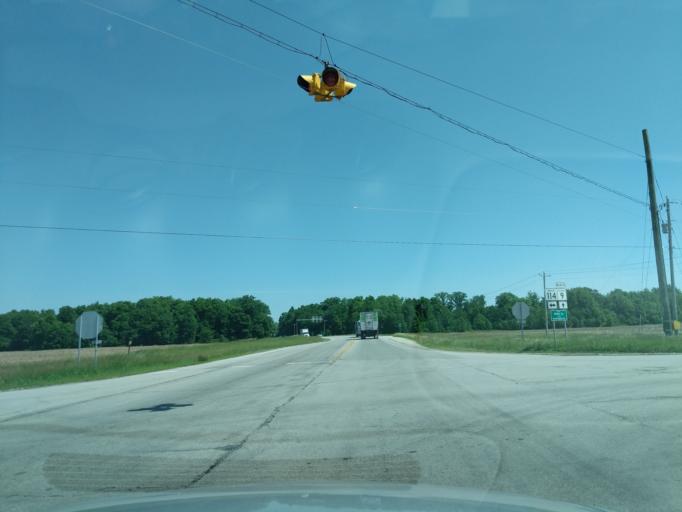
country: US
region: Indiana
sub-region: Huntington County
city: Roanoke
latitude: 41.0044
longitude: -85.4713
